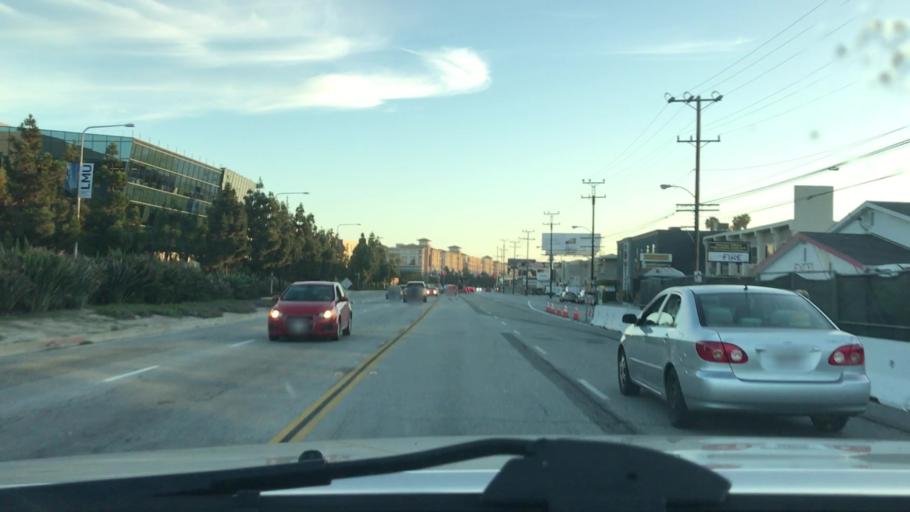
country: US
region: California
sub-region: Los Angeles County
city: Ladera Heights
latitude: 33.9835
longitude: -118.4057
